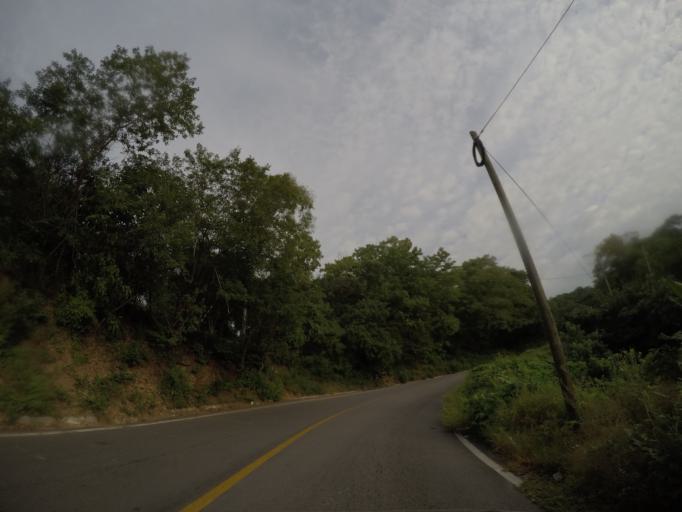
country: MX
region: Oaxaca
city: San Pedro Pochutla
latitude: 15.7021
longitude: -96.4821
